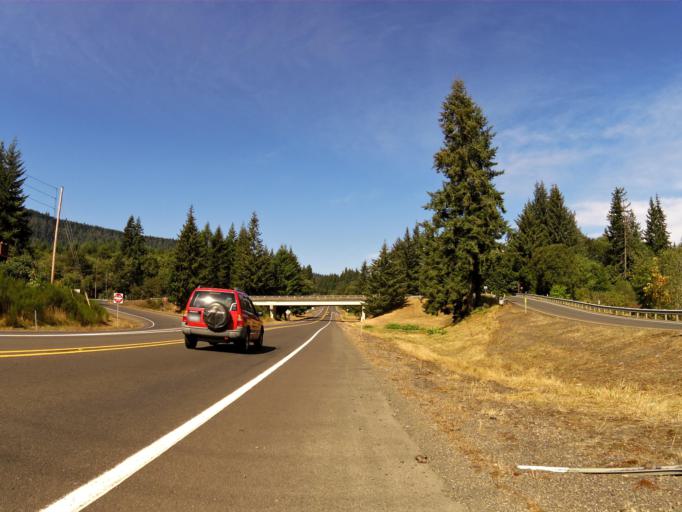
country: US
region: Washington
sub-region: Wahkiakum County
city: Cathlamet
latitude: 46.1494
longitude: -123.4074
